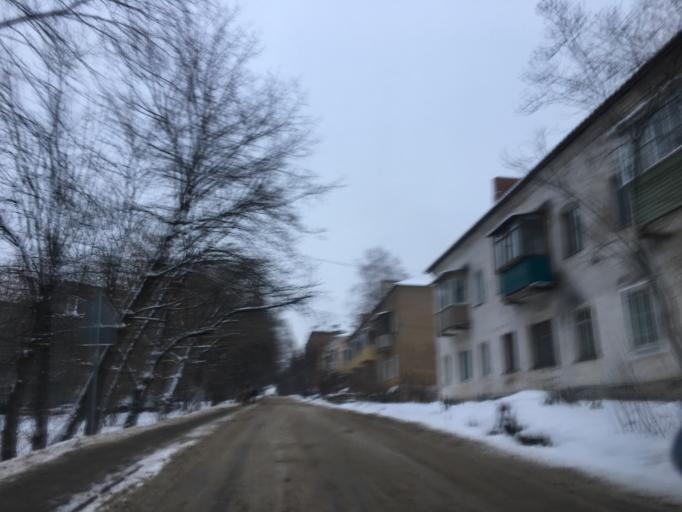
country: RU
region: Tula
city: Mendeleyevskiy
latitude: 54.1659
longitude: 37.5694
